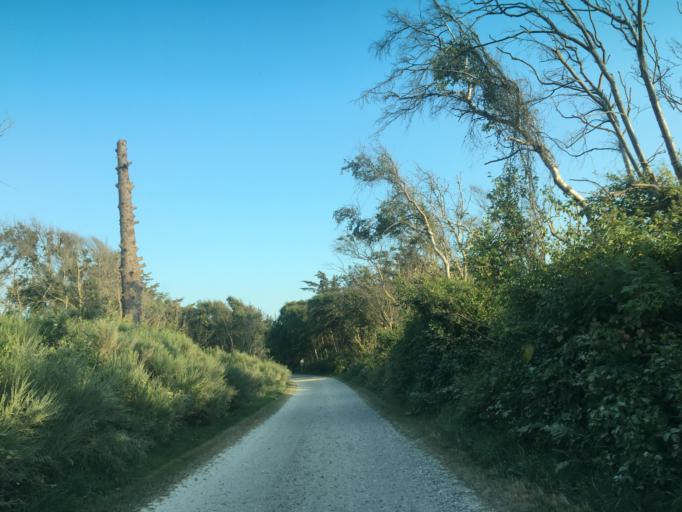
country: DK
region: Central Jutland
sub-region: Lemvig Kommune
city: Thyboron
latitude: 56.8227
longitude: 8.2633
